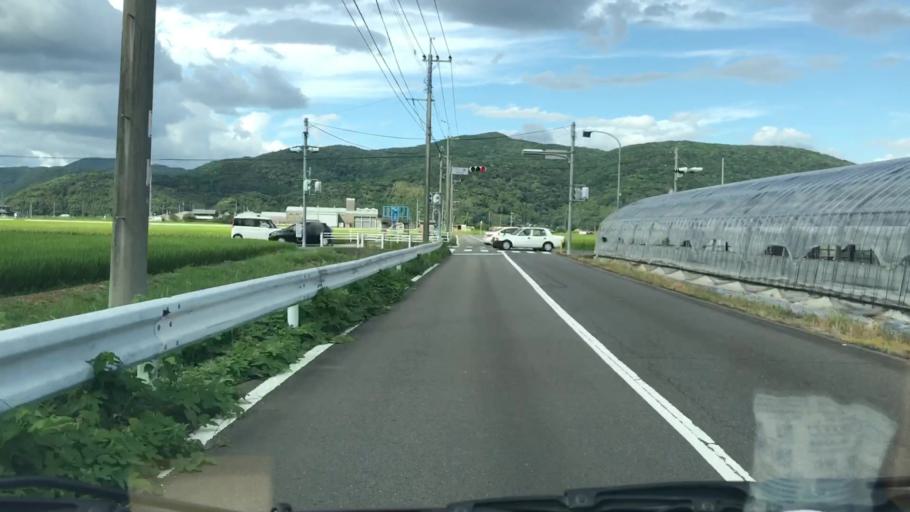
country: JP
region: Saga Prefecture
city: Kashima
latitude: 33.1192
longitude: 130.0704
